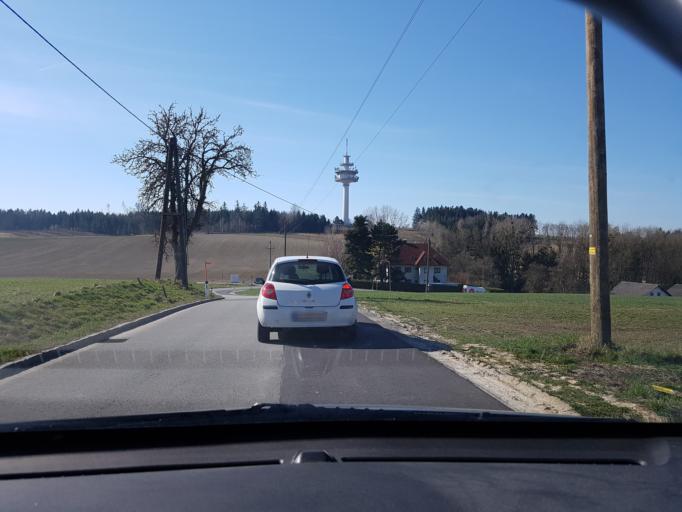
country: AT
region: Upper Austria
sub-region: Politischer Bezirk Linz-Land
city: Ansfelden
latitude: 48.2069
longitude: 14.2966
